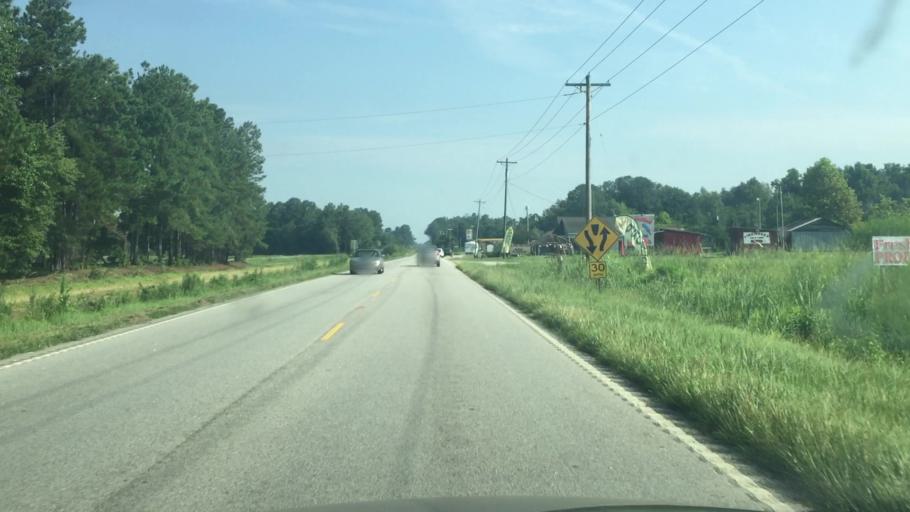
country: US
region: North Carolina
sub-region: Columbus County
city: Tabor City
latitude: 34.1298
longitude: -78.8760
